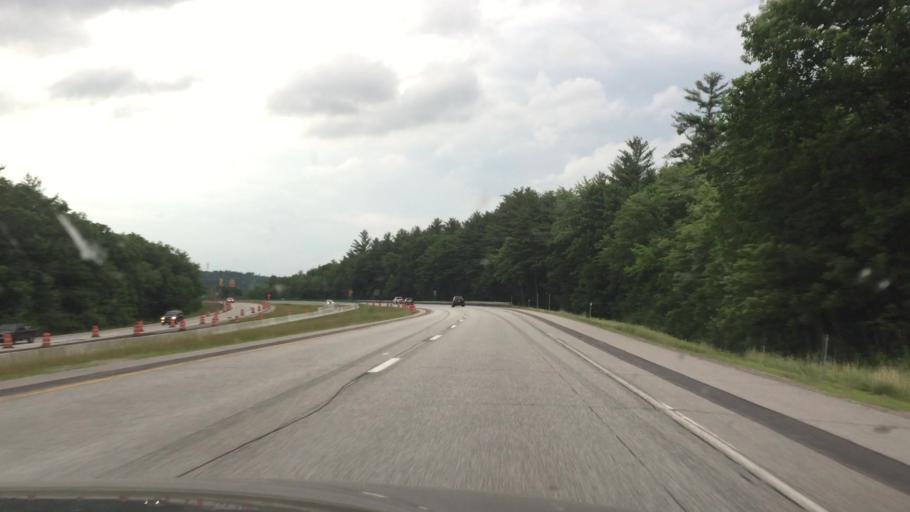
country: US
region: New Hampshire
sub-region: Belknap County
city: Tilton
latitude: 43.4476
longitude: -71.5717
